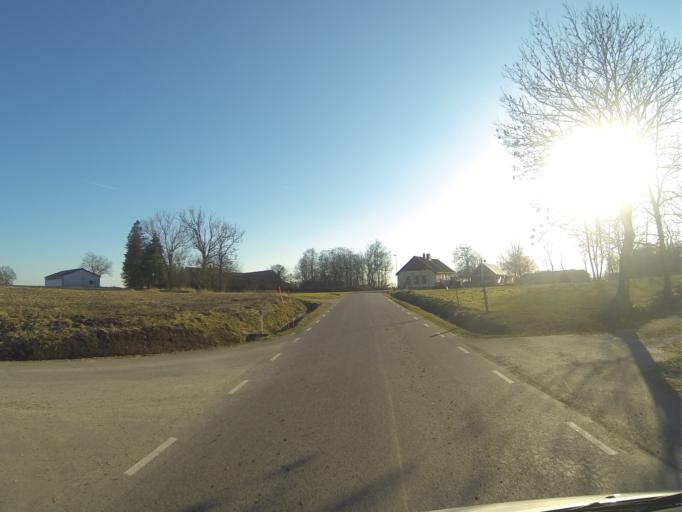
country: SE
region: Skane
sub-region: Hoors Kommun
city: Loberod
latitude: 55.7509
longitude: 13.4631
